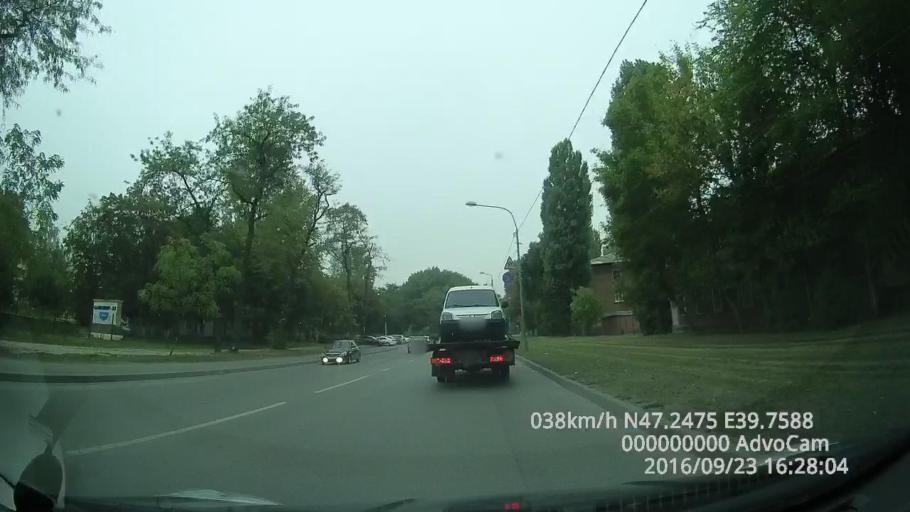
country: RU
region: Rostov
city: Imeni Chkalova
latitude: 47.2474
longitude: 39.7588
